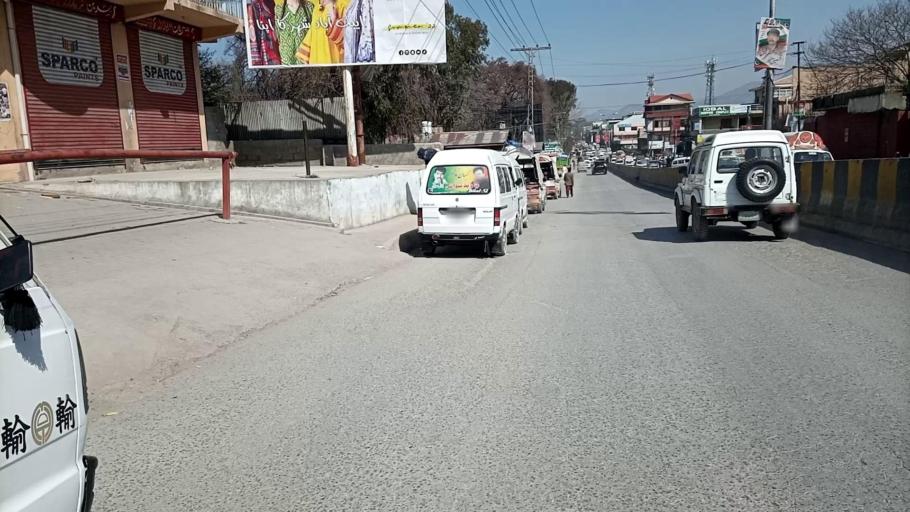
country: PK
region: Khyber Pakhtunkhwa
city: Abbottabad
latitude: 34.1429
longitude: 73.2142
